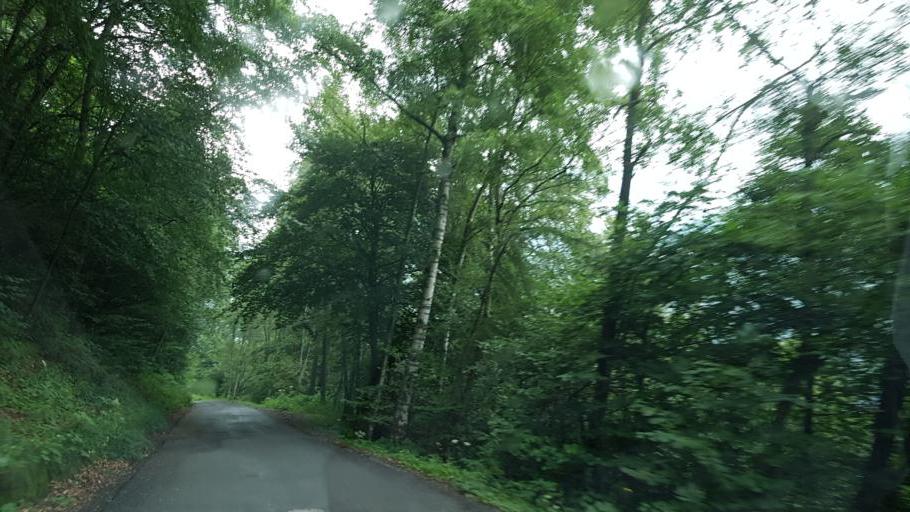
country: IT
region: Piedmont
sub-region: Provincia di Cuneo
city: Sampeyre
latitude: 44.5737
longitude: 7.1737
